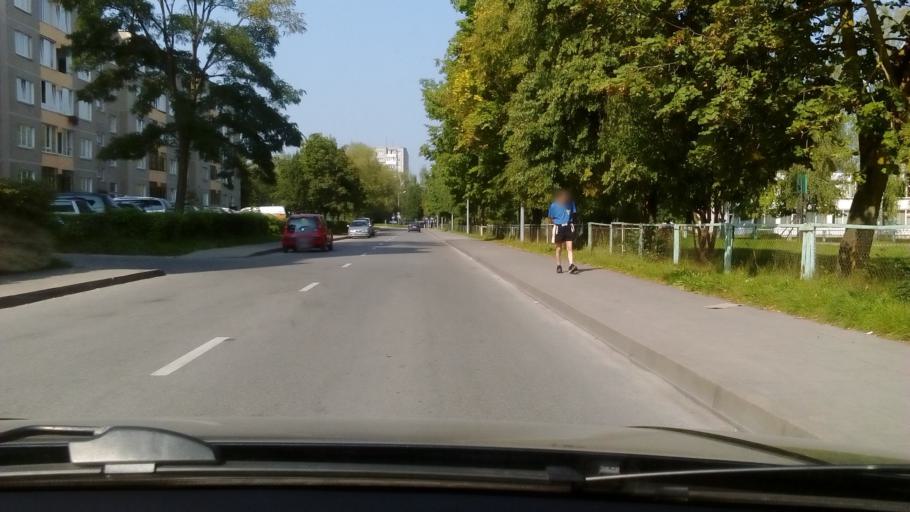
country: LT
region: Alytaus apskritis
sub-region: Alytus
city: Alytus
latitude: 54.3929
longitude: 24.0227
